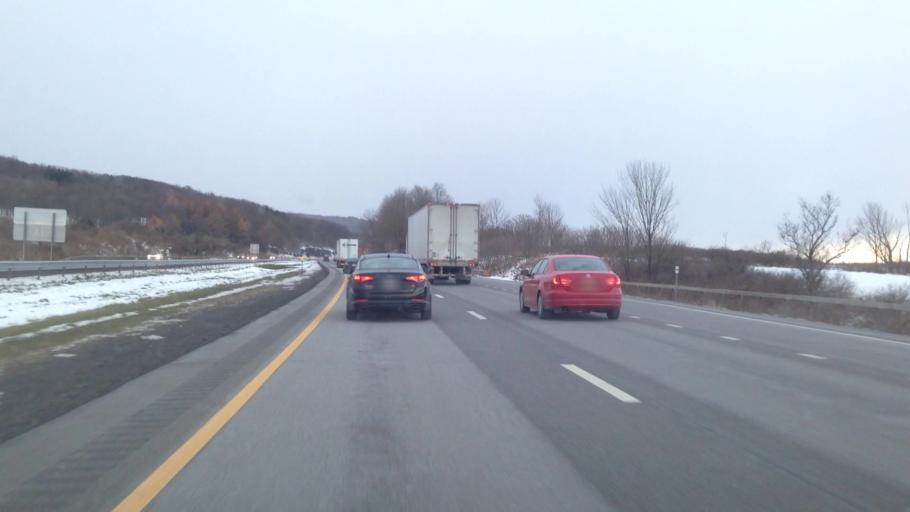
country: US
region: New York
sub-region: Herkimer County
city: Little Falls
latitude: 43.0147
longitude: -74.8268
